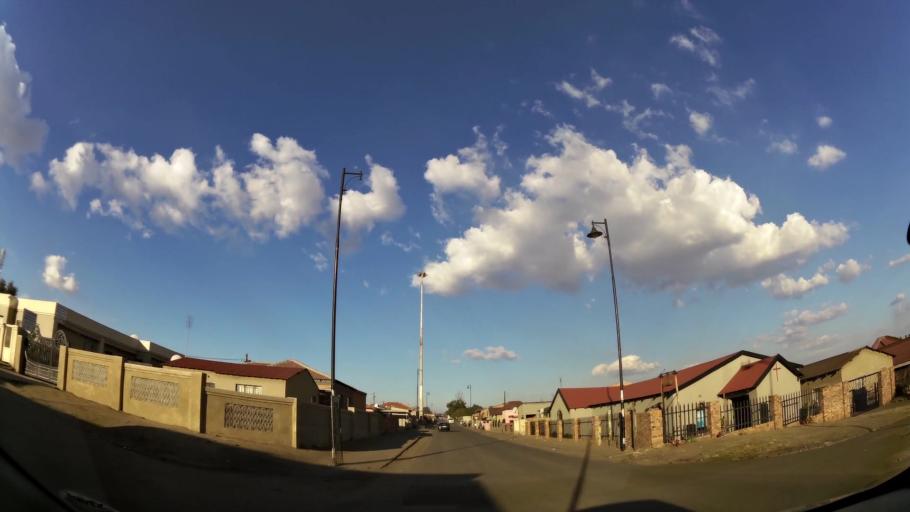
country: ZA
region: Mpumalanga
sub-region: Nkangala District Municipality
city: Witbank
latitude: -25.8723
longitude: 29.1893
